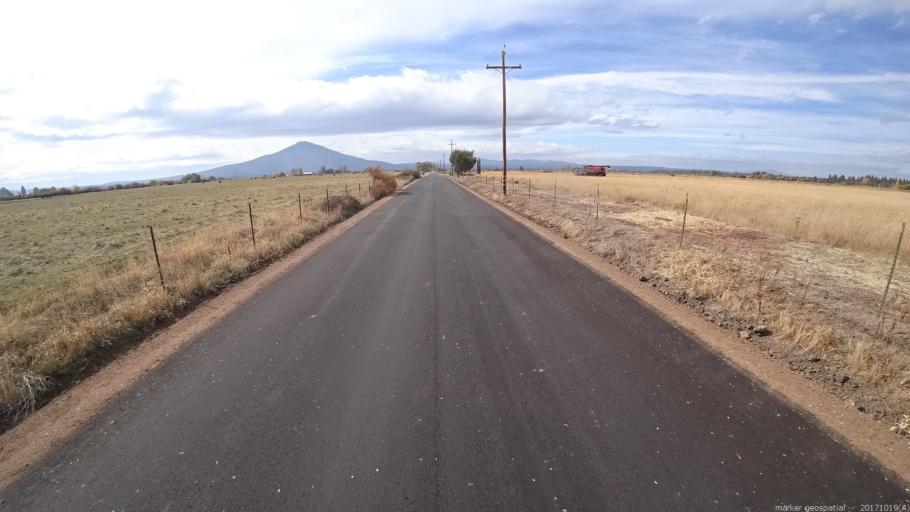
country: US
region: California
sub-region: Shasta County
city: Burney
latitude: 41.0979
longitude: -121.4766
